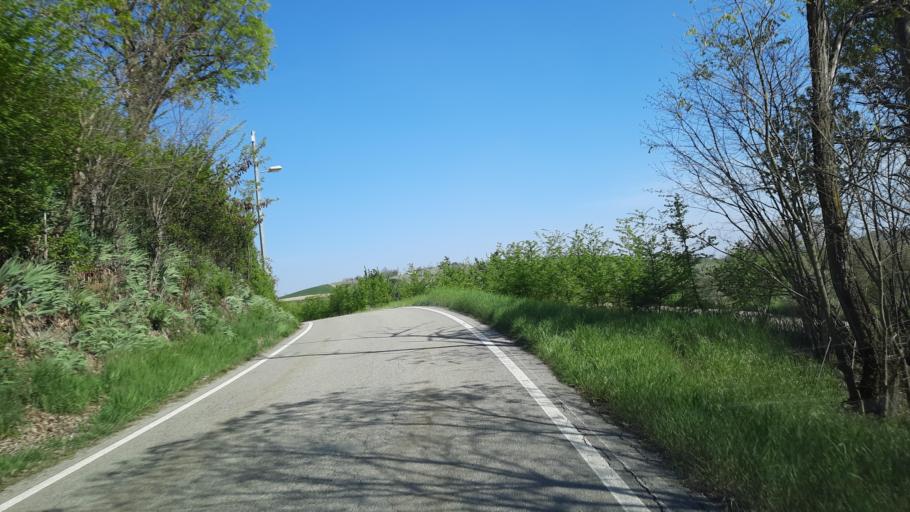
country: IT
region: Piedmont
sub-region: Provincia di Alessandria
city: Vignale Monferrato
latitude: 45.0168
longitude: 8.4091
